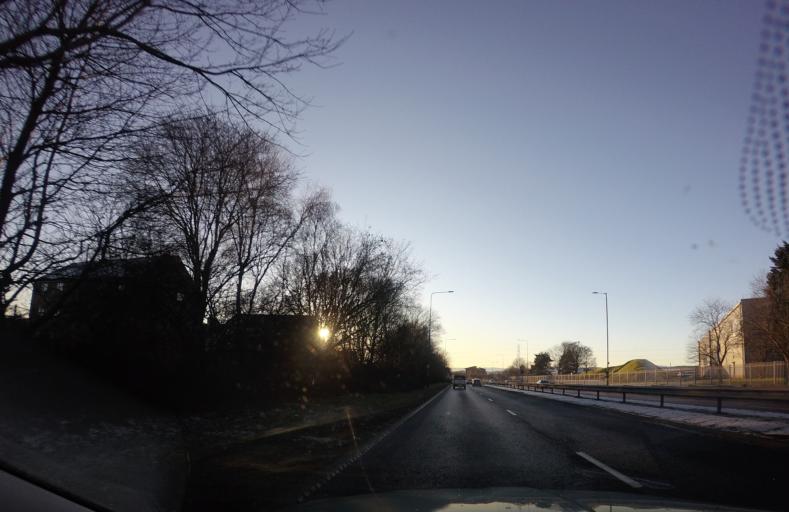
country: GB
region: Scotland
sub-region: Angus
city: Muirhead
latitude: 56.4760
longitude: -3.0414
